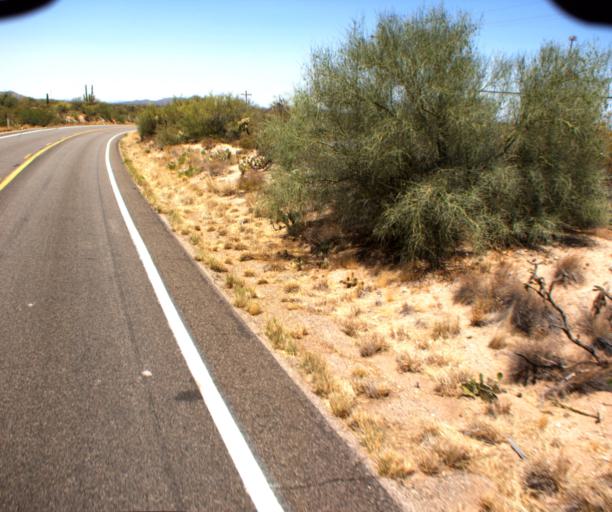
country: US
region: Arizona
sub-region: Pima County
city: Catalina
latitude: 32.6738
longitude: -111.0659
